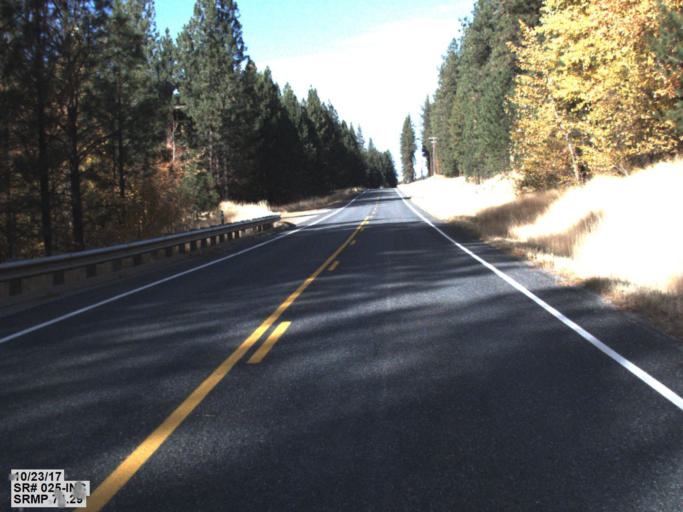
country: US
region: Washington
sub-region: Stevens County
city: Kettle Falls
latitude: 48.5308
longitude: -118.1349
